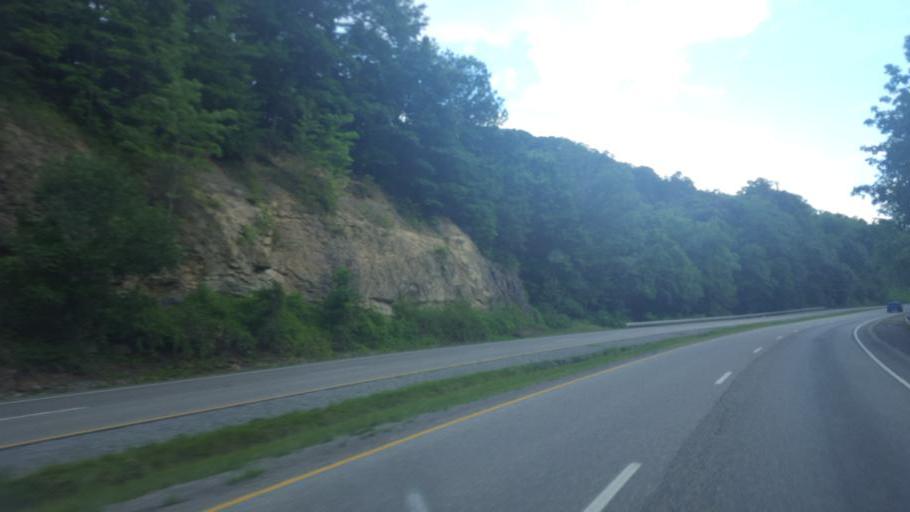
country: US
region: Virginia
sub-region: Wise County
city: Wise
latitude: 37.0267
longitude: -82.5933
